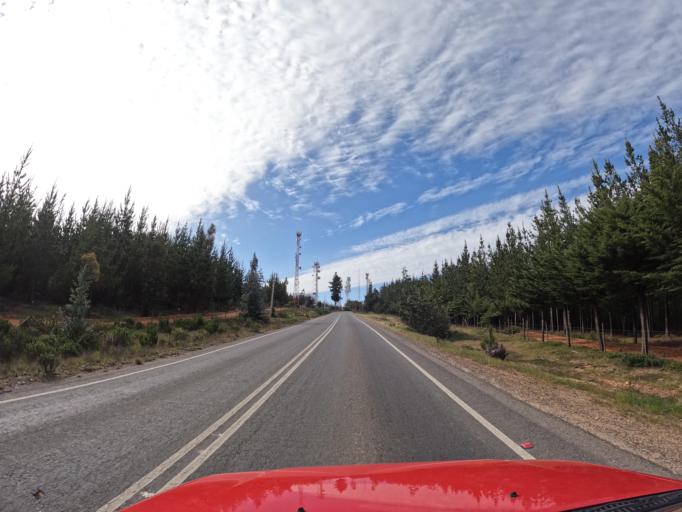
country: CL
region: O'Higgins
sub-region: Provincia de Colchagua
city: Santa Cruz
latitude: -34.3366
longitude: -71.8751
